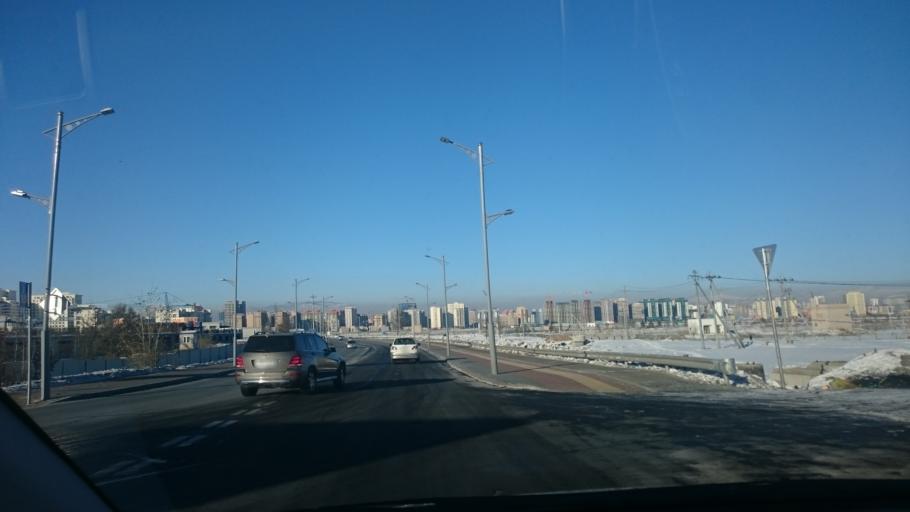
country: MN
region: Ulaanbaatar
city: Ulaanbaatar
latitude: 47.8891
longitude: 106.9389
